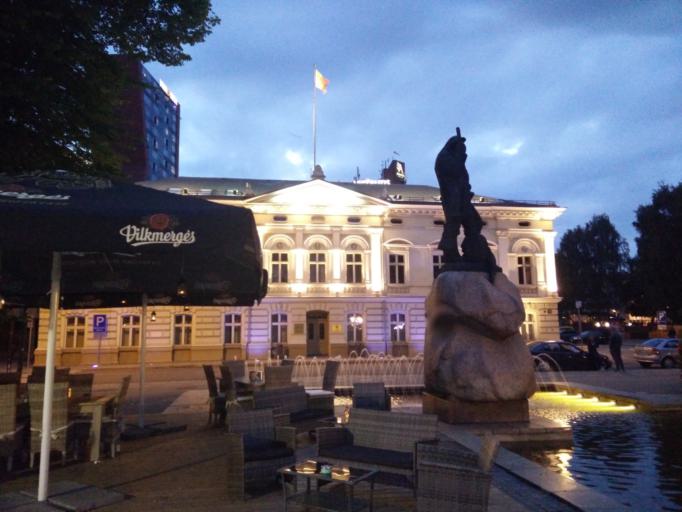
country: LT
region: Klaipedos apskritis
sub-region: Klaipeda
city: Klaipeda
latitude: 55.7098
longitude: 21.1315
